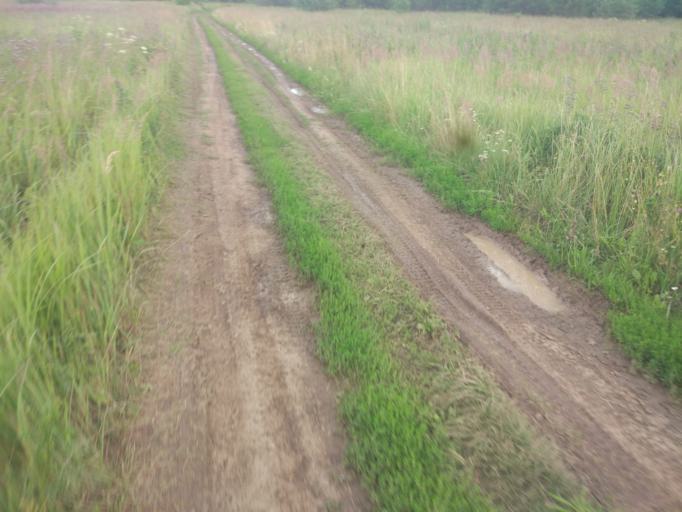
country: RU
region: Vladimir
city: Krasnyy Oktyabr'
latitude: 56.0344
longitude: 38.9254
